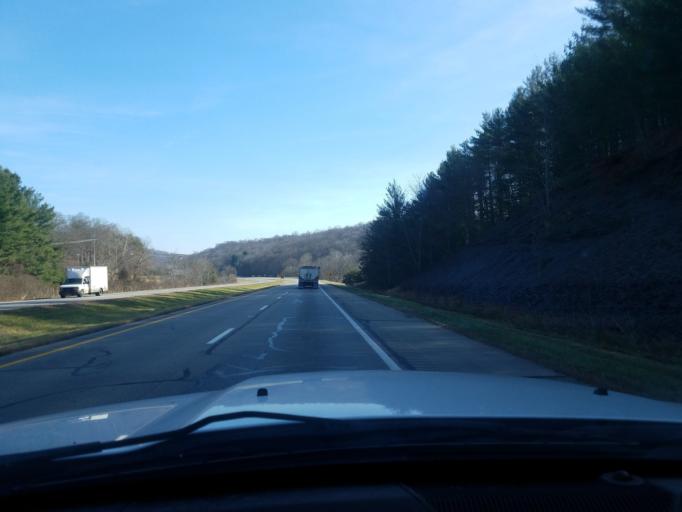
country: US
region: Ohio
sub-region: Pike County
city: Piketon
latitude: 39.0603
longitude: -83.1015
